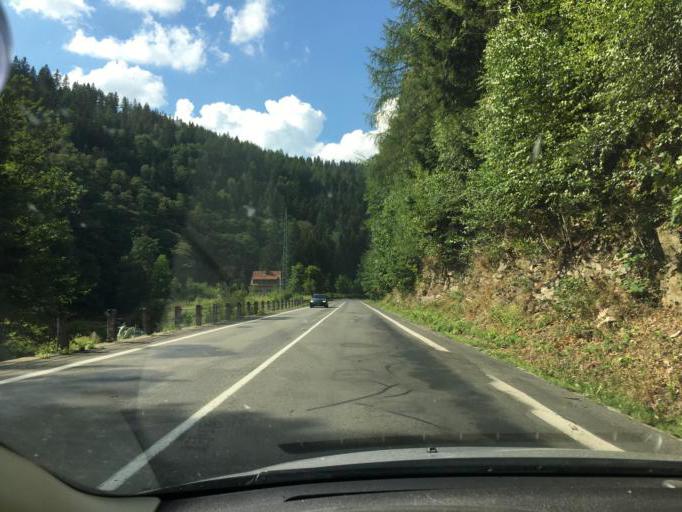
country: CZ
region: Kralovehradecky
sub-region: Okres Trutnov
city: Vrchlabi
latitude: 50.6676
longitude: 15.5937
